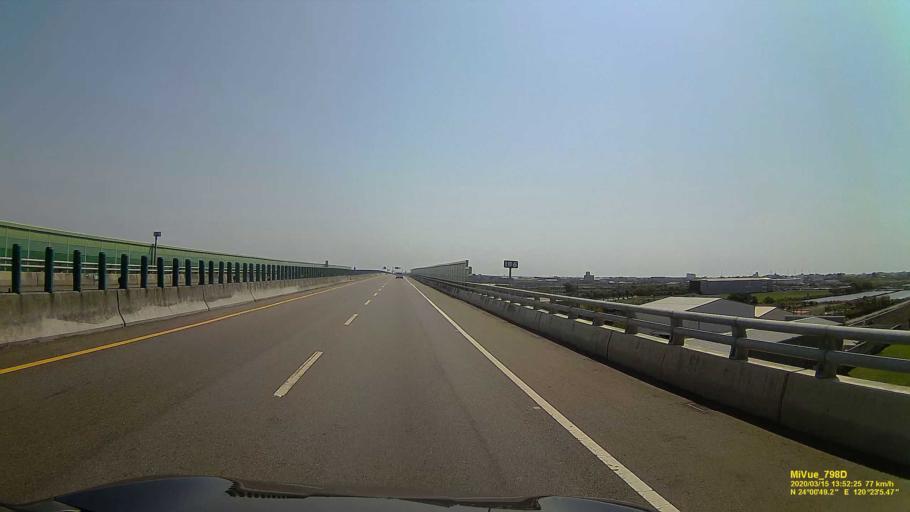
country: TW
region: Taiwan
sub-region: Changhua
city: Chang-hua
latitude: 24.0133
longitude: 120.3847
